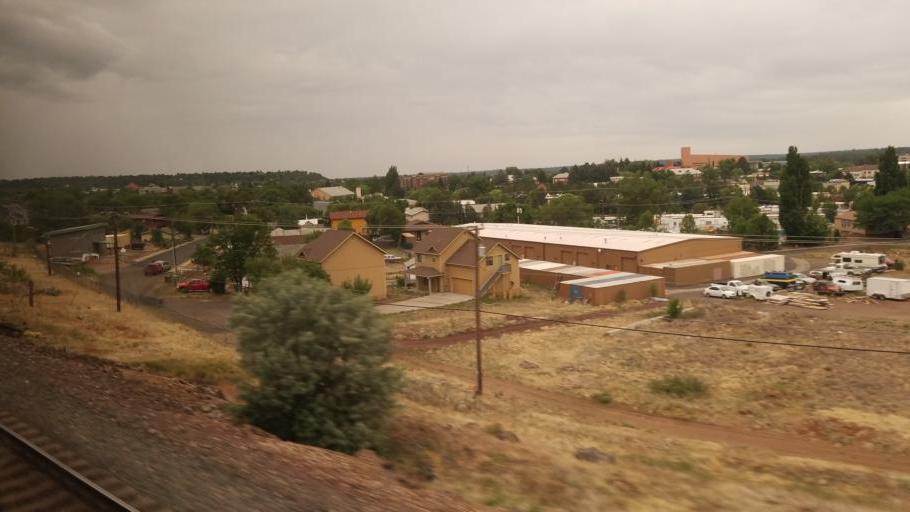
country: US
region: Arizona
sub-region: Coconino County
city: Flagstaff
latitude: 35.1956
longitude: -111.6634
